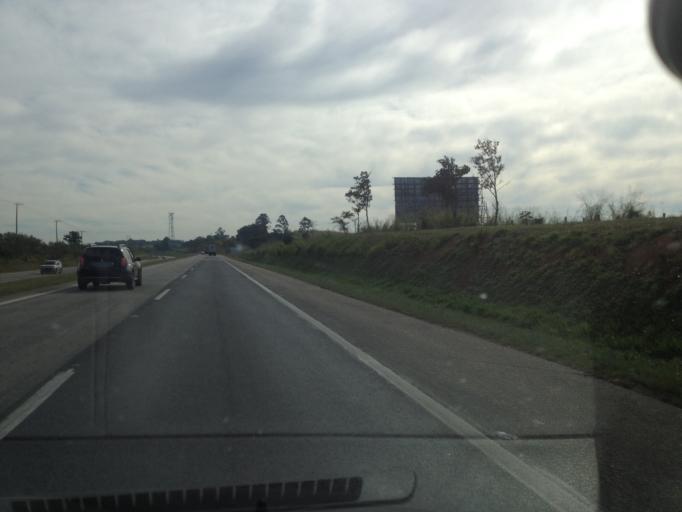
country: BR
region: Sao Paulo
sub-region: Itu
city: Itu
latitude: -23.3401
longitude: -47.3243
